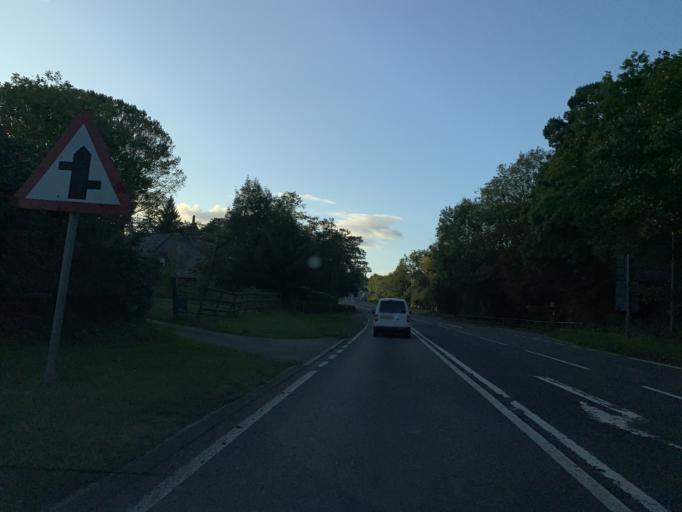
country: GB
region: England
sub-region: Wiltshire
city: Whiteparish
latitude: 50.9783
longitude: -1.6305
